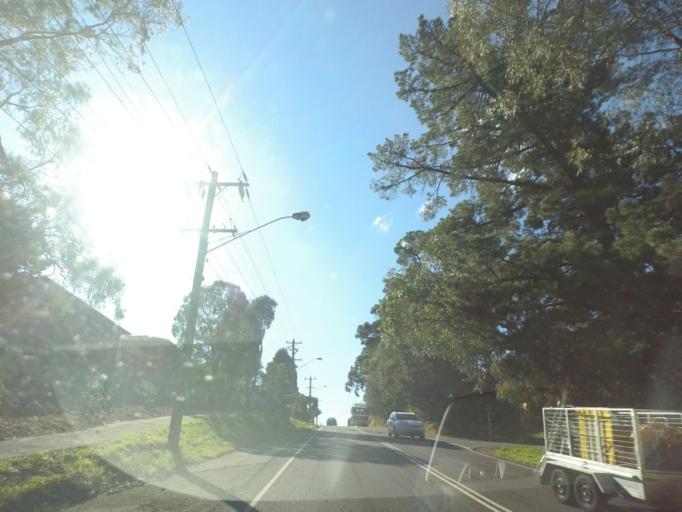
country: AU
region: Victoria
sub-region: Manningham
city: Donvale
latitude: -37.7749
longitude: 145.1830
